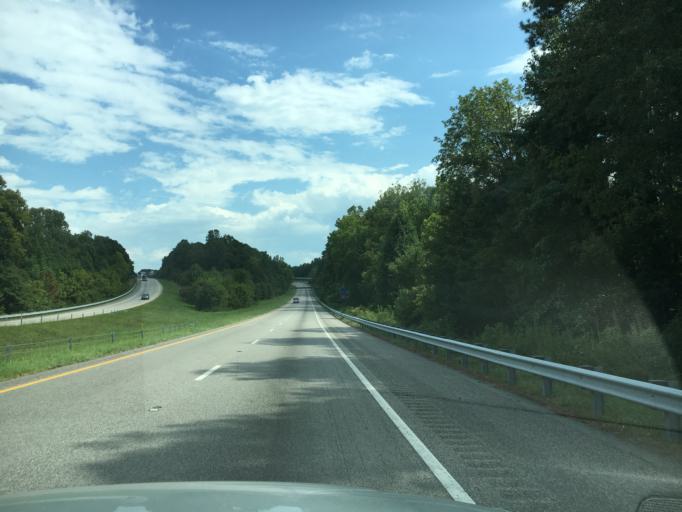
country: US
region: South Carolina
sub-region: Laurens County
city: Clinton
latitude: 34.5174
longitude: -81.8731
